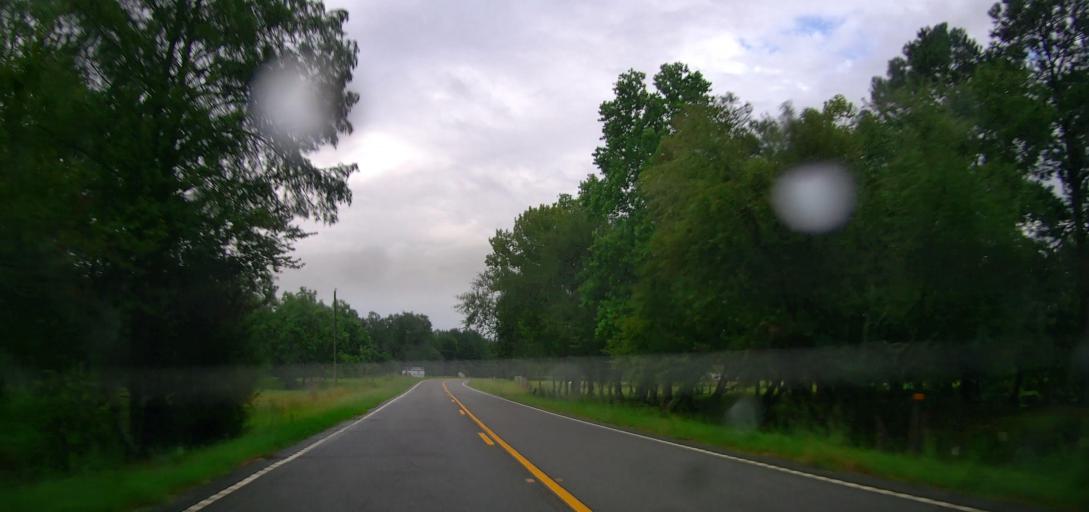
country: US
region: Georgia
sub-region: Ware County
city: Deenwood
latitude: 31.2699
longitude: -82.4039
